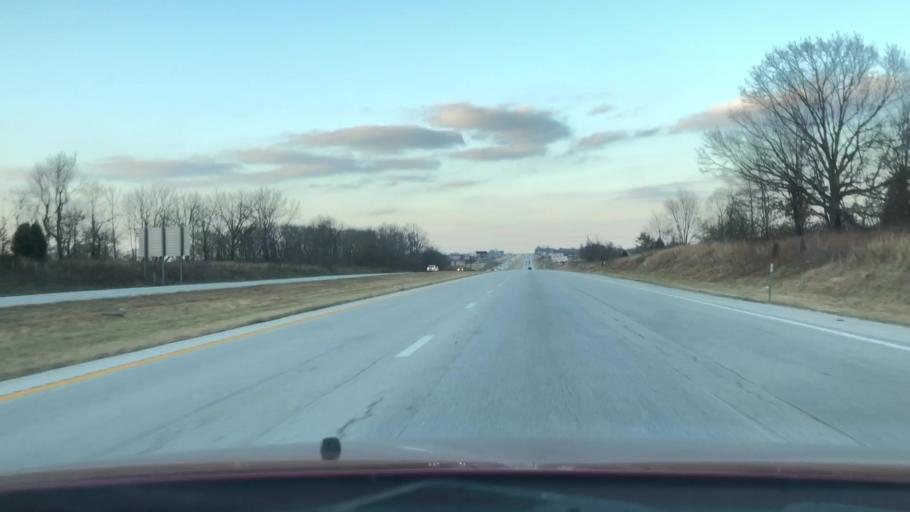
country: US
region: Missouri
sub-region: Christian County
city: Ozark
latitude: 36.9469
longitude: -93.2318
